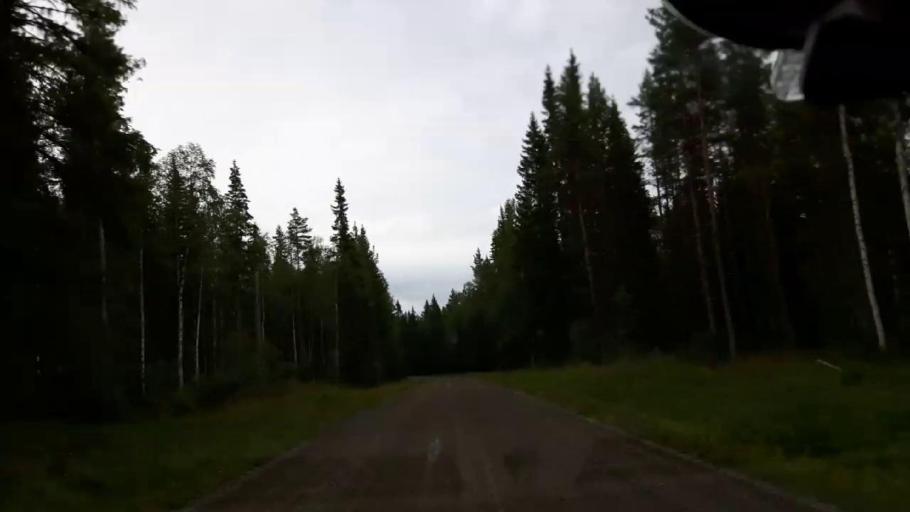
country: SE
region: Jaemtland
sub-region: Braecke Kommun
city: Braecke
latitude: 62.9213
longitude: 15.5508
